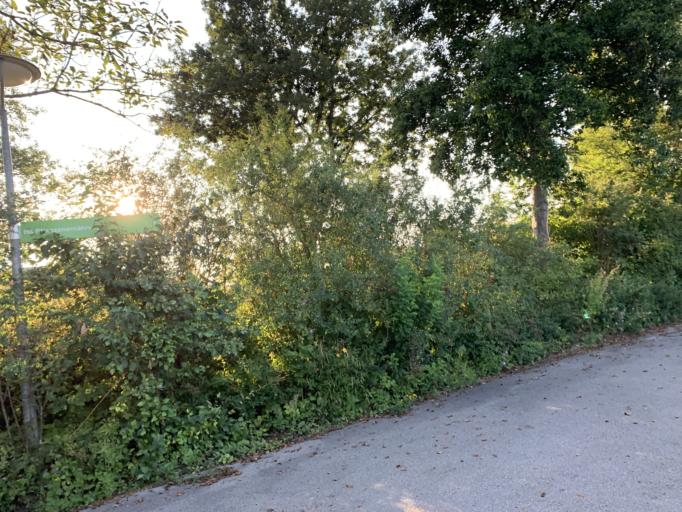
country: DE
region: Bavaria
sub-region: Upper Bavaria
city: Freising
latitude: 48.4028
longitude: 11.7301
